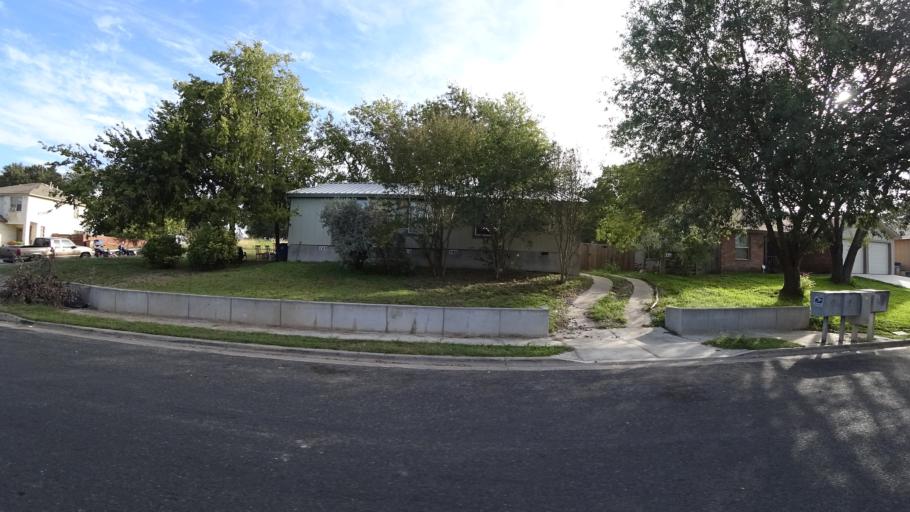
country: US
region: Texas
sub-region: Travis County
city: Austin
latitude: 30.1941
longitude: -97.7306
